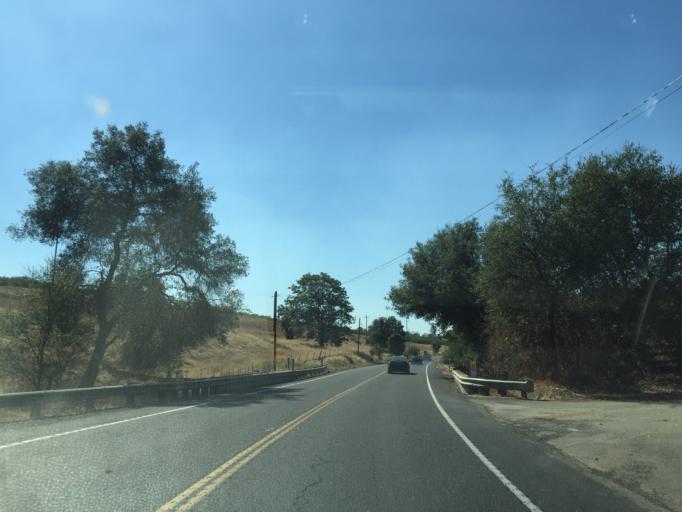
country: US
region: California
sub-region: Stanislaus County
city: East Oakdale
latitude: 37.7924
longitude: -120.7254
